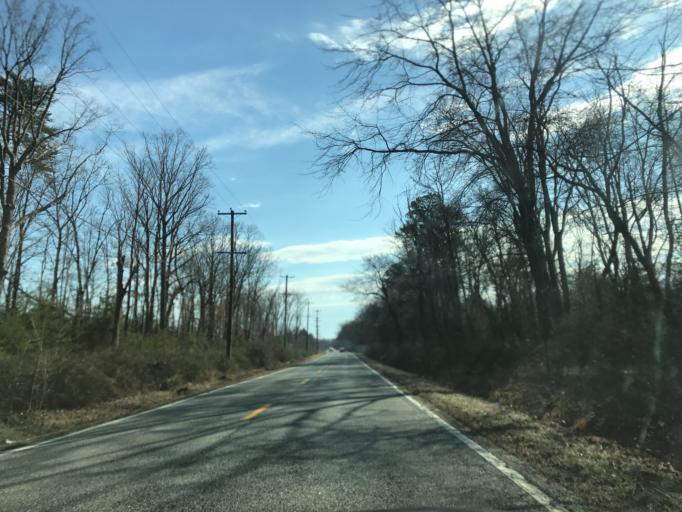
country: US
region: Maryland
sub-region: Cecil County
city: Charlestown
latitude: 39.5810
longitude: -76.0048
